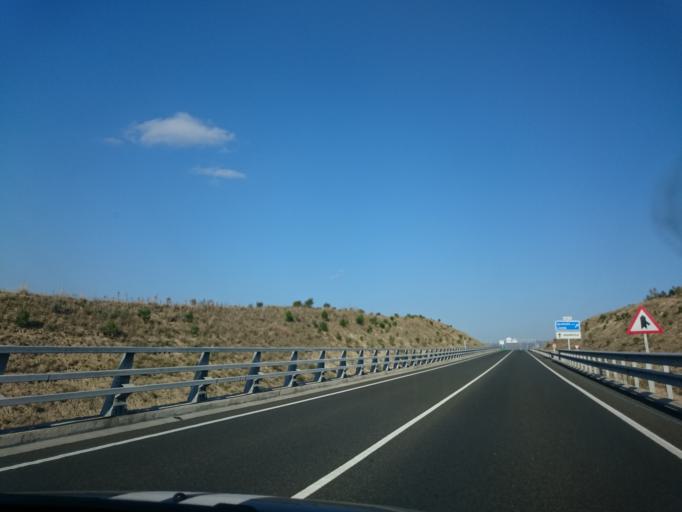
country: ES
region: Catalonia
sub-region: Provincia de Barcelona
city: Odena
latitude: 41.5802
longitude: 1.6685
